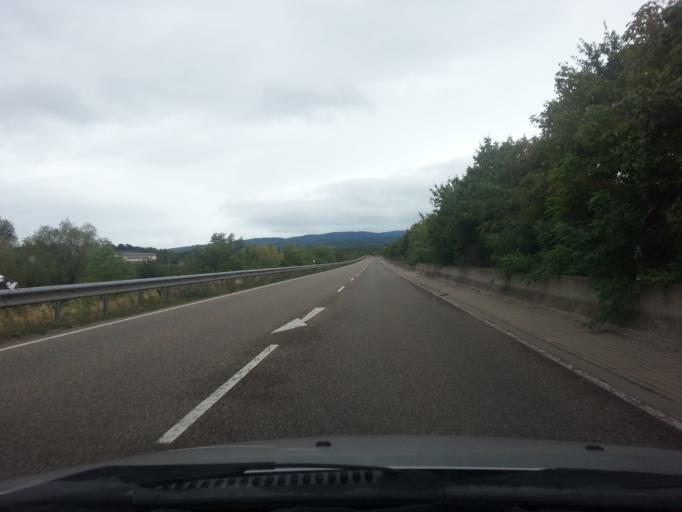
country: DE
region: Rheinland-Pfalz
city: Bad Duerkheim
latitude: 49.4665
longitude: 8.1934
